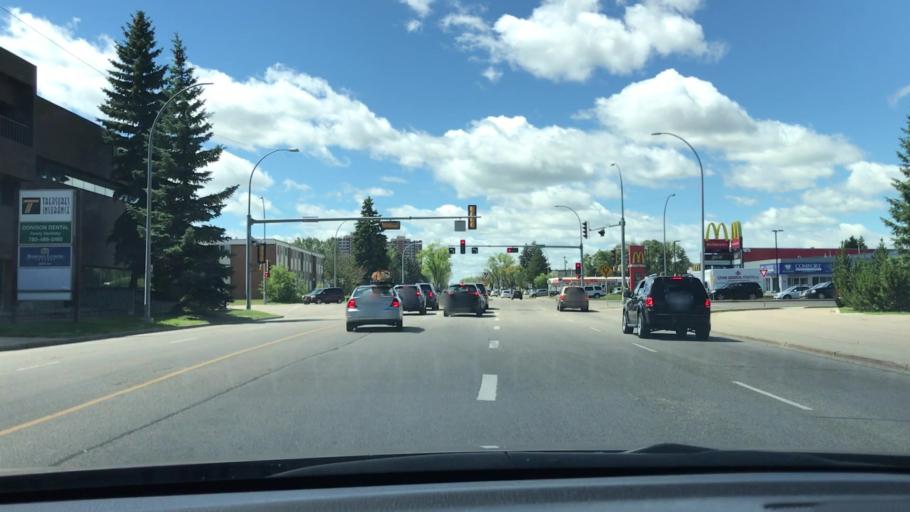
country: CA
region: Alberta
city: Edmonton
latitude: 53.5194
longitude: -113.5768
